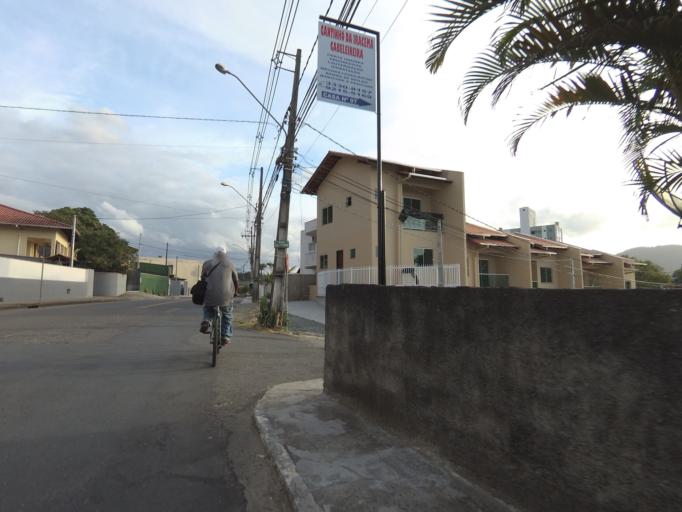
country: BR
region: Santa Catarina
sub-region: Blumenau
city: Blumenau
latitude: -26.8960
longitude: -49.1280
